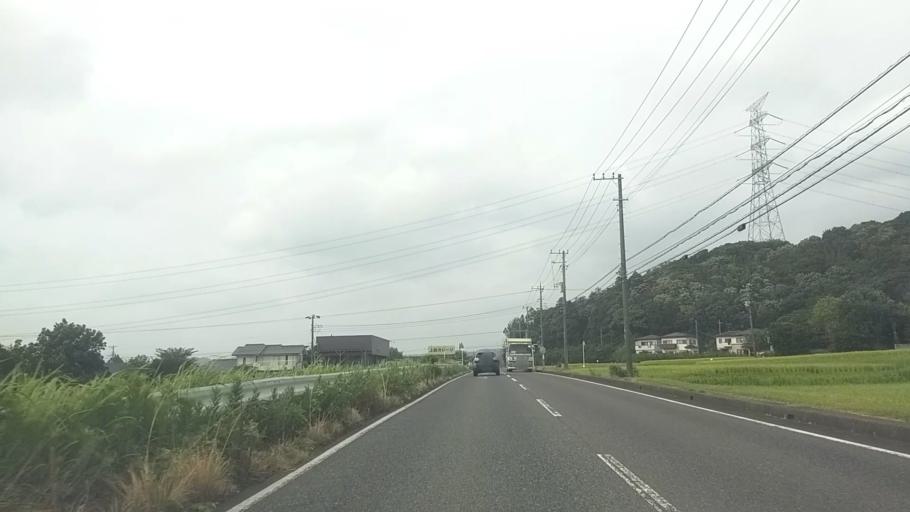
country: JP
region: Chiba
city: Kimitsu
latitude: 35.2817
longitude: 139.9901
